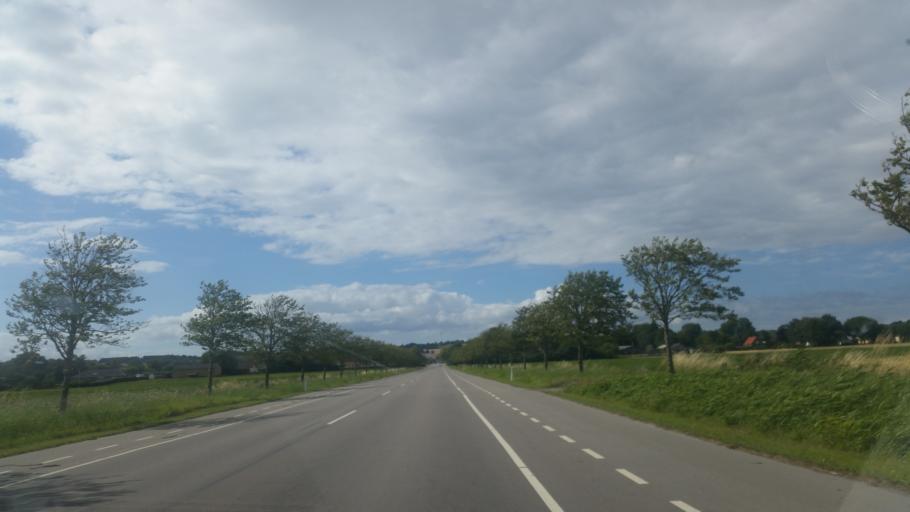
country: DK
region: Zealand
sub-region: Odsherred Kommune
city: Horve
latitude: 55.7971
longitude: 11.4501
